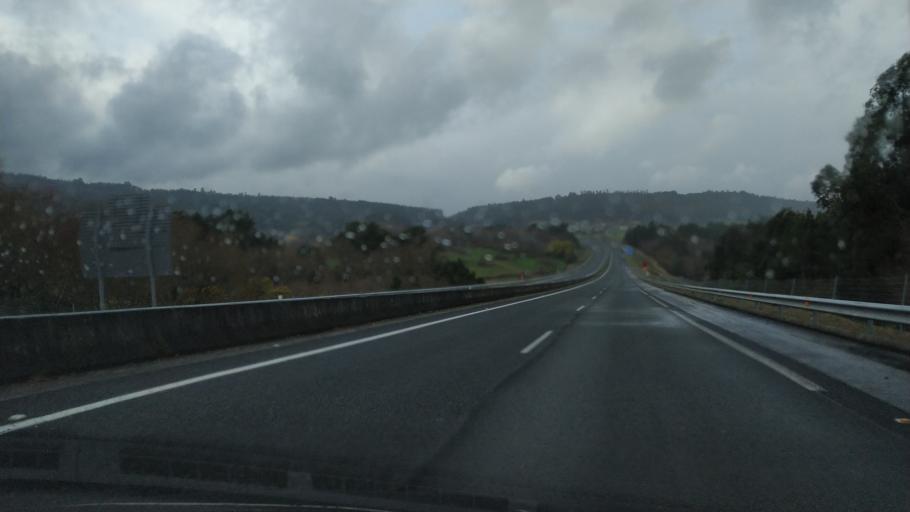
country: ES
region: Galicia
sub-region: Provincia de Pontevedra
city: Silleda
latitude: 42.7246
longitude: -8.3185
